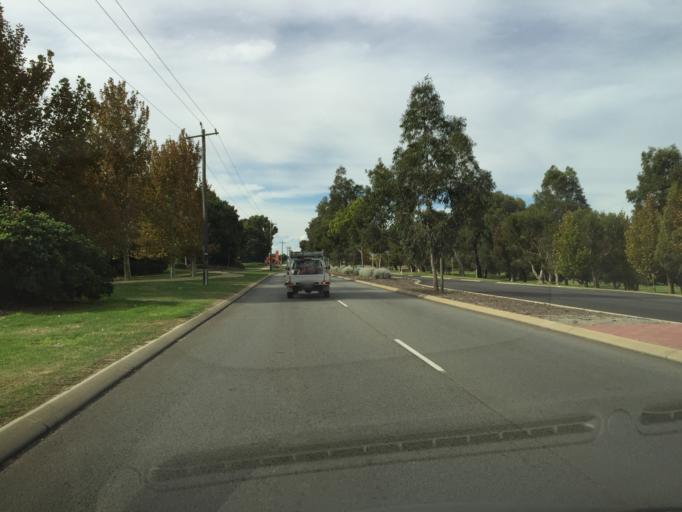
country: AU
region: Western Australia
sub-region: Canning
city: Willetton
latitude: -32.0691
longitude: 115.8964
